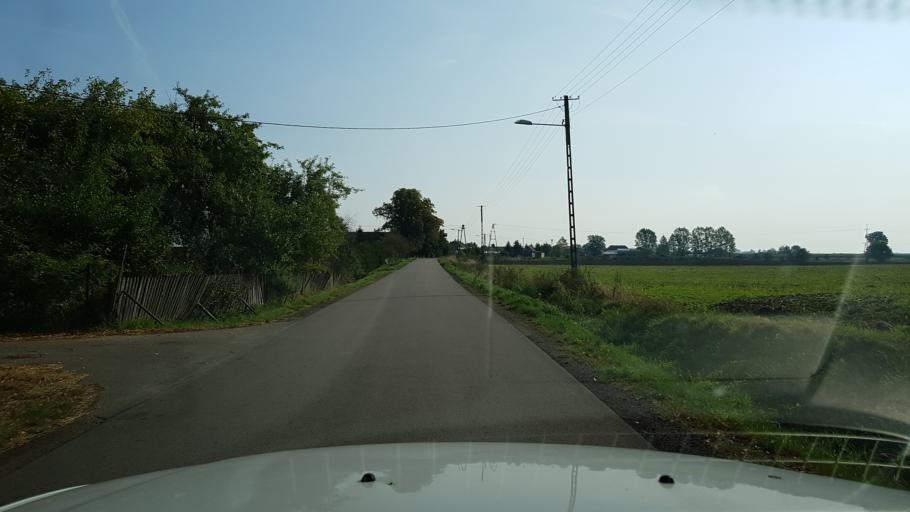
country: PL
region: West Pomeranian Voivodeship
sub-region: Powiat slawienski
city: Slawno
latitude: 54.3644
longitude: 16.5438
